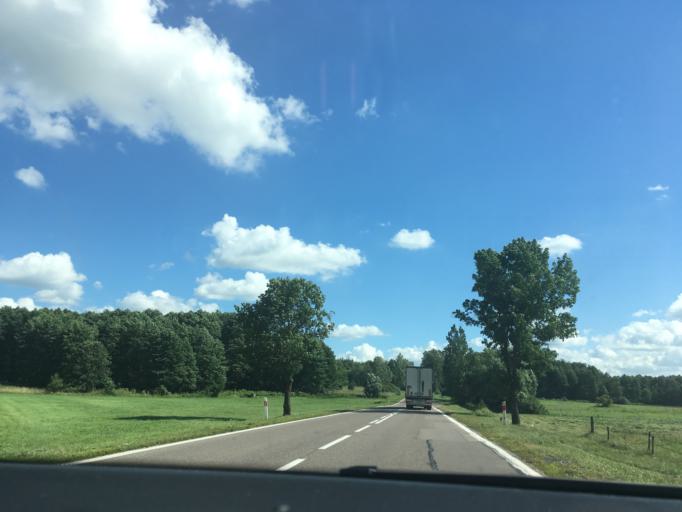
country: PL
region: Podlasie
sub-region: Powiat sokolski
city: Suchowola
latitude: 53.6255
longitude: 23.1227
